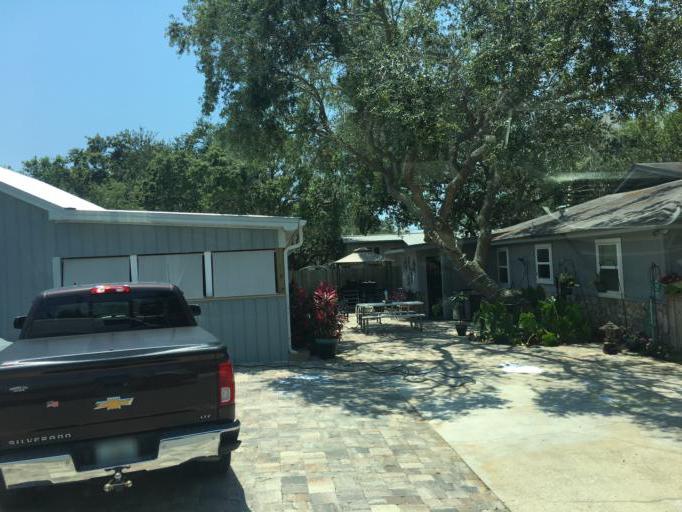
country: US
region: Florida
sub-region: Bay County
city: Panama City Beach
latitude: 30.2052
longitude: -85.8524
